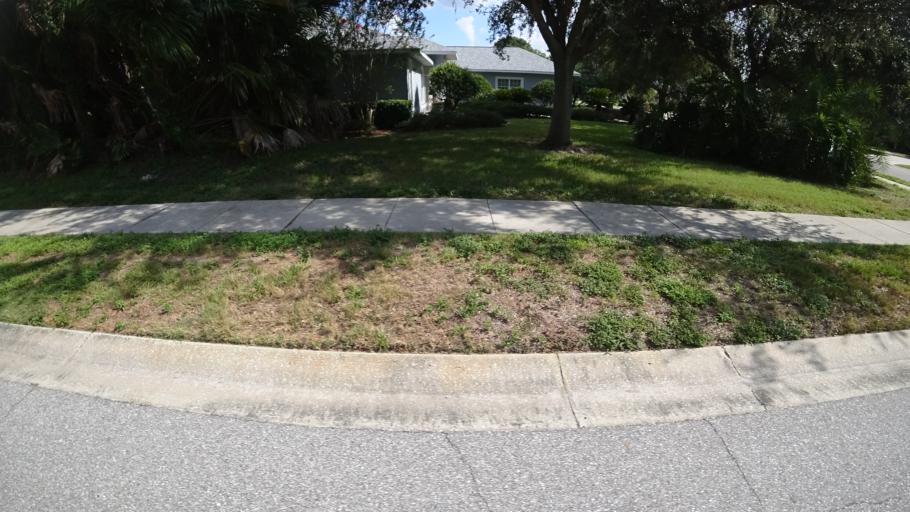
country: US
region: Florida
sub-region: Sarasota County
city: The Meadows
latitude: 27.4286
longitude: -82.4403
